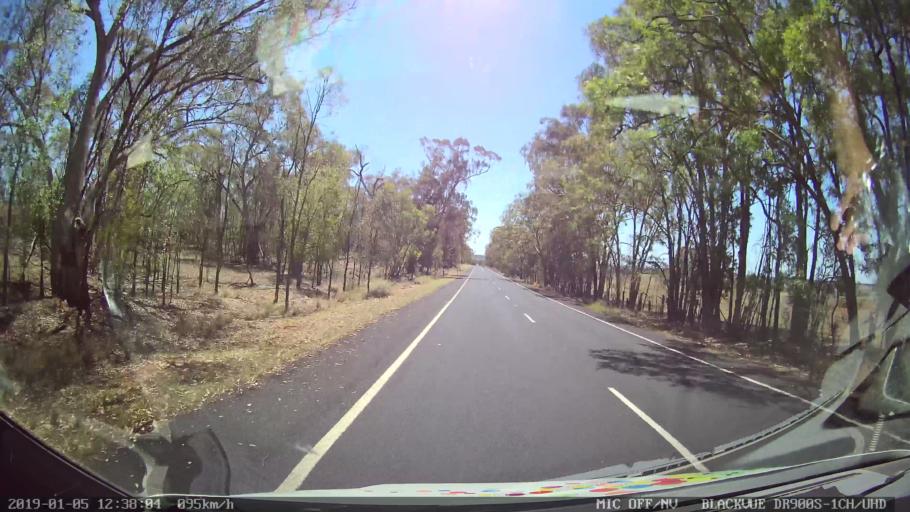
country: AU
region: New South Wales
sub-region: Warrumbungle Shire
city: Coonabarabran
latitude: -31.1987
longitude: 149.4633
